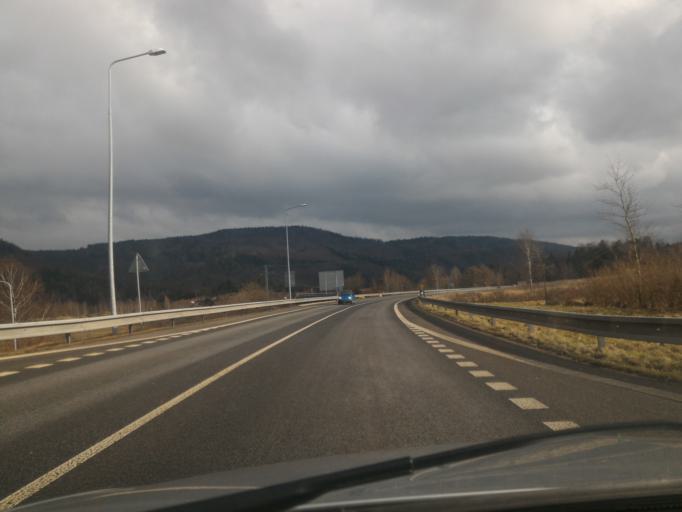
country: CZ
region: Liberecky
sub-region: Okres Liberec
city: Liberec
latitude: 50.7573
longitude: 15.1037
